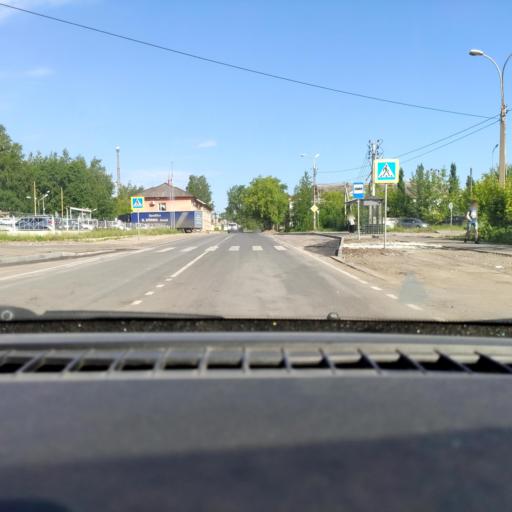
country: RU
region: Perm
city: Krasnokamsk
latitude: 58.0772
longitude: 55.7770
